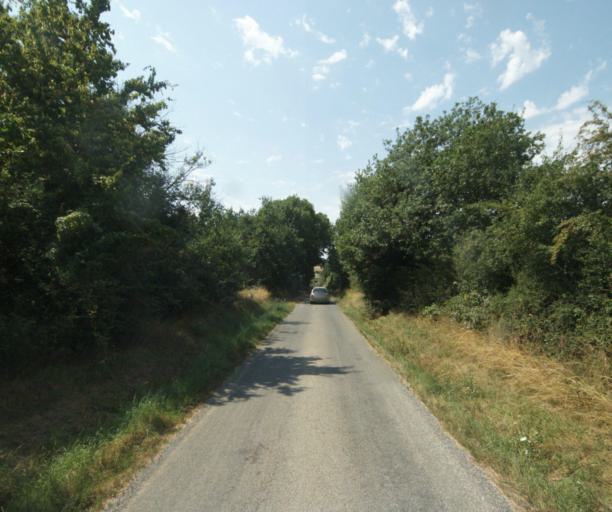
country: FR
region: Rhone-Alpes
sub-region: Departement du Rhone
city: Sourcieux-les-Mines
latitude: 45.8308
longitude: 4.6308
